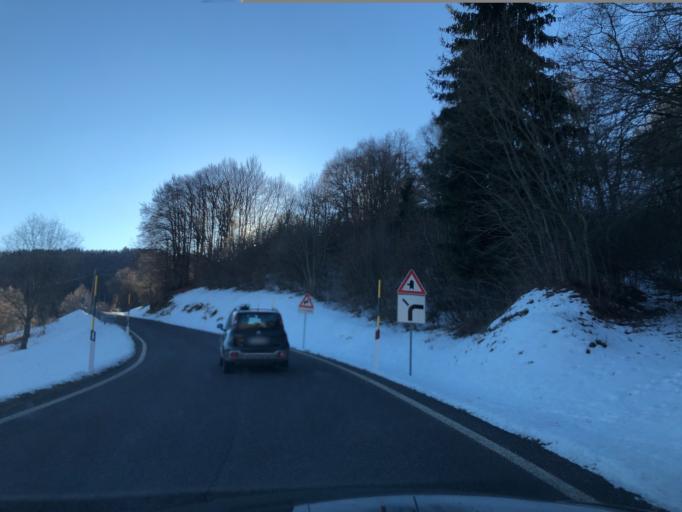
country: IT
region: Trentino-Alto Adige
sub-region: Provincia di Trento
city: Brentonico
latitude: 45.7909
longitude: 10.9163
